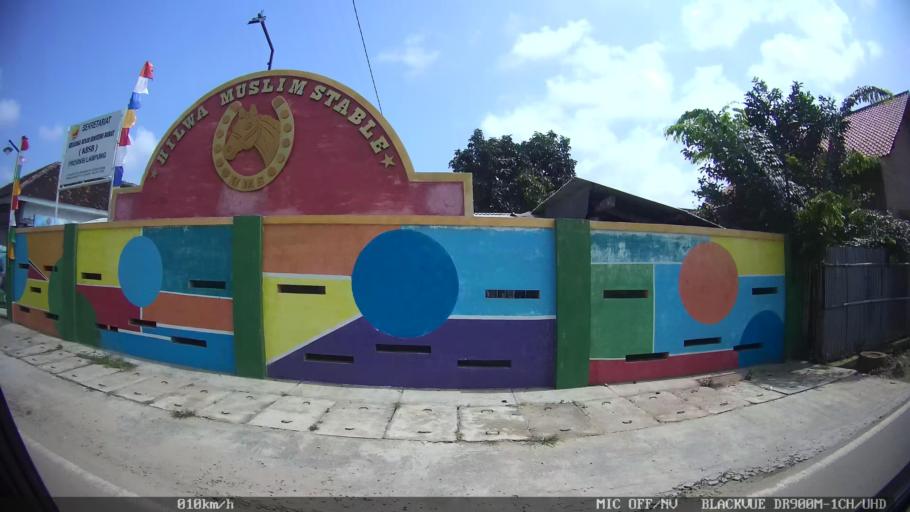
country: ID
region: Lampung
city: Kedaton
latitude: -5.3505
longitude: 105.2893
